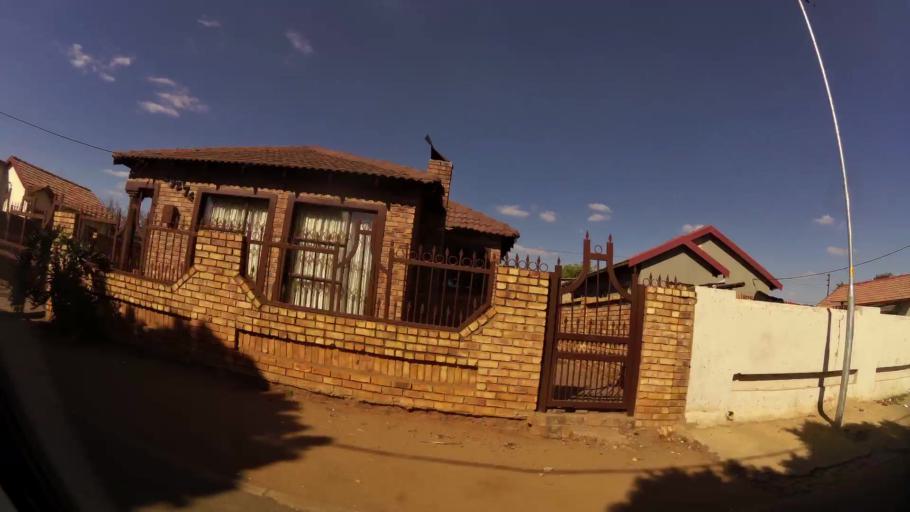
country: ZA
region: Gauteng
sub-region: City of Tshwane Metropolitan Municipality
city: Cullinan
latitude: -25.7154
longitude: 28.4027
